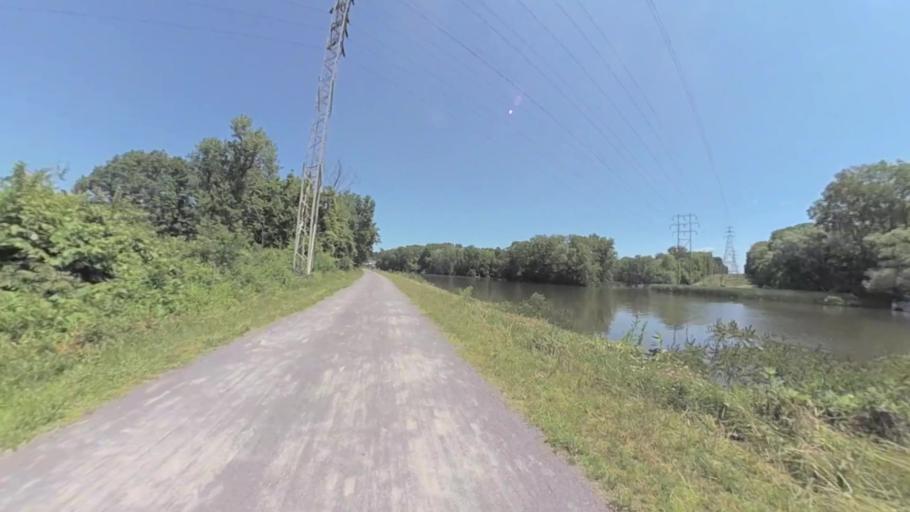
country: US
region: New York
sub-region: Monroe County
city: Fairport
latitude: 43.0872
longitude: -77.4567
